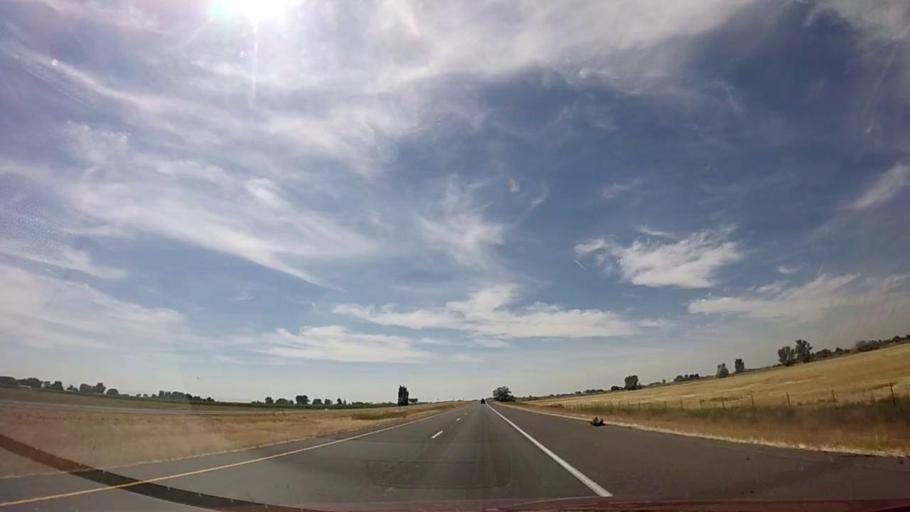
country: US
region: Idaho
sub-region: Minidoka County
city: Rupert
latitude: 42.5690
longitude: -113.6554
